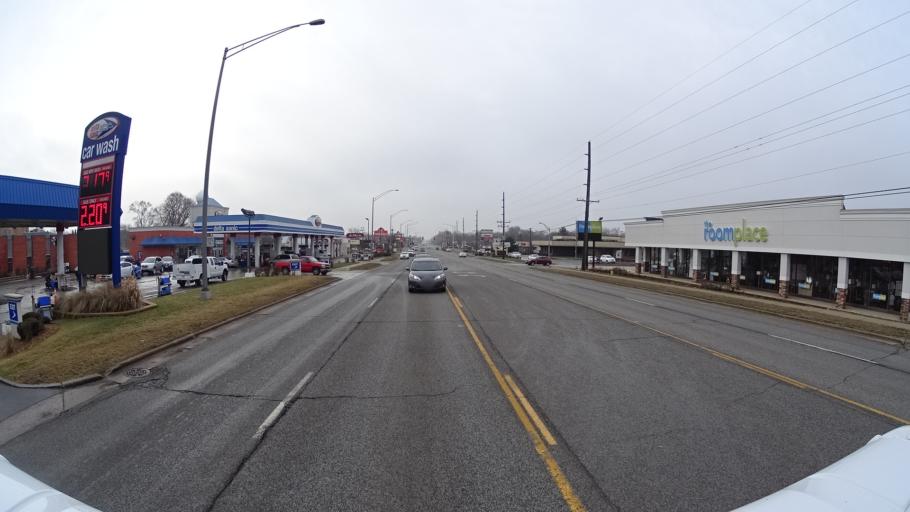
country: US
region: Illinois
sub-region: Cook County
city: East Hazel Crest
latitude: 41.5598
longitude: -87.6360
